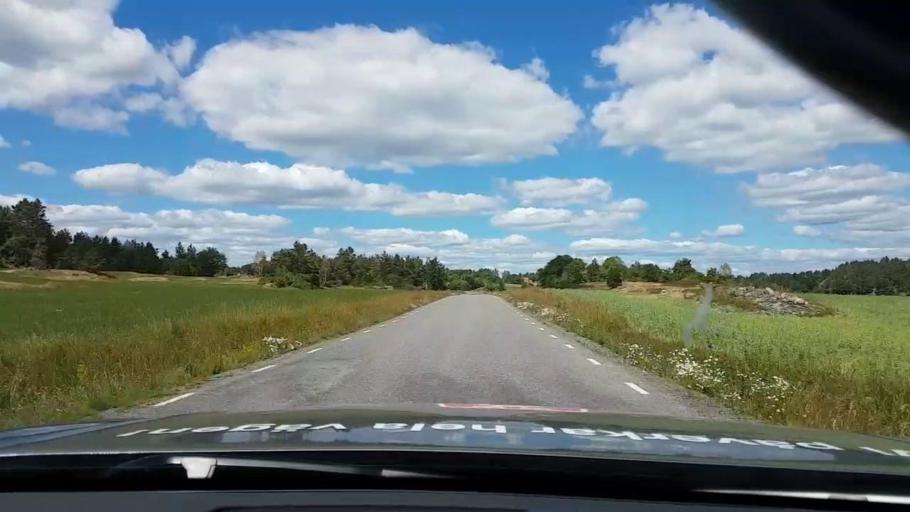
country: SE
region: Kalmar
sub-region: Vasterviks Kommun
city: Forserum
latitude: 58.0033
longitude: 16.5888
